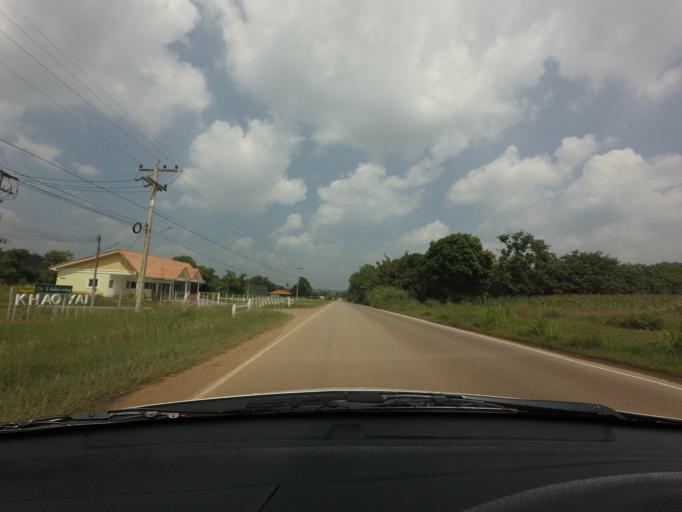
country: TH
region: Nakhon Ratchasima
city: Pak Chong
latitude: 14.5569
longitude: 101.5730
